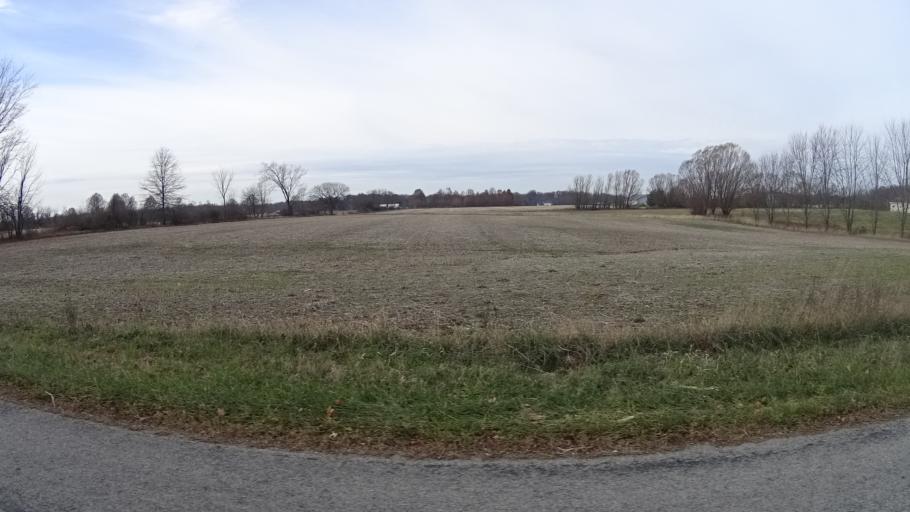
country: US
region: Ohio
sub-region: Lorain County
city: Eaton Estates
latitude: 41.2569
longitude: -81.9729
